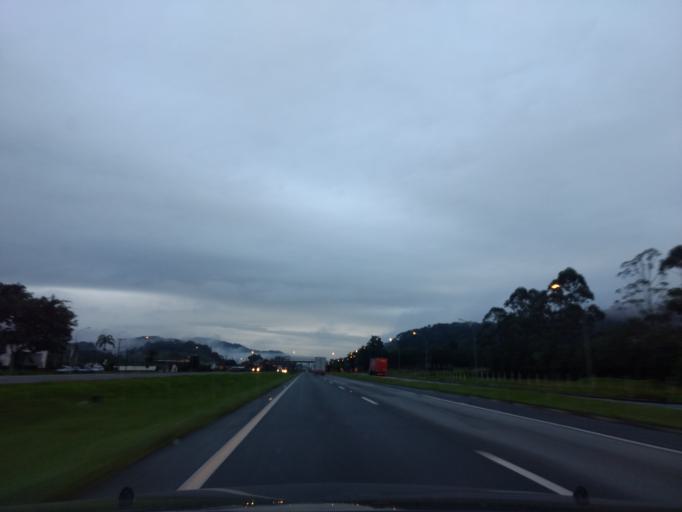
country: BR
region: Sao Paulo
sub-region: Juquia
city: Juquia
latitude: -24.3416
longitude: -47.6460
